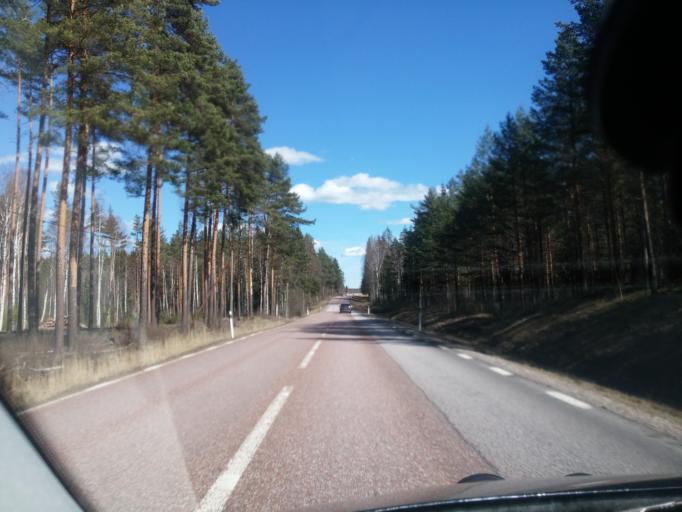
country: SE
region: Dalarna
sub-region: Faluns Kommun
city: Svardsjo
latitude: 60.7083
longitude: 15.7581
